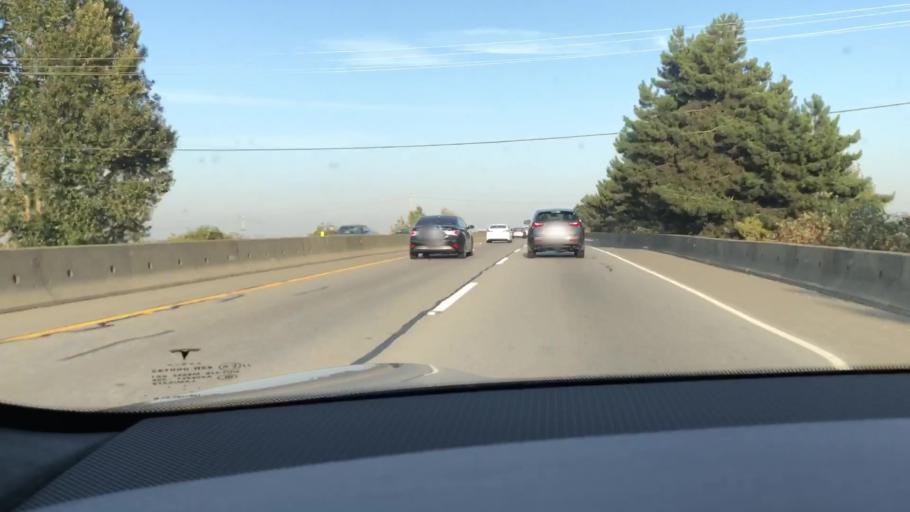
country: CA
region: British Columbia
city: New Westminster
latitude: 49.1699
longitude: -123.0030
